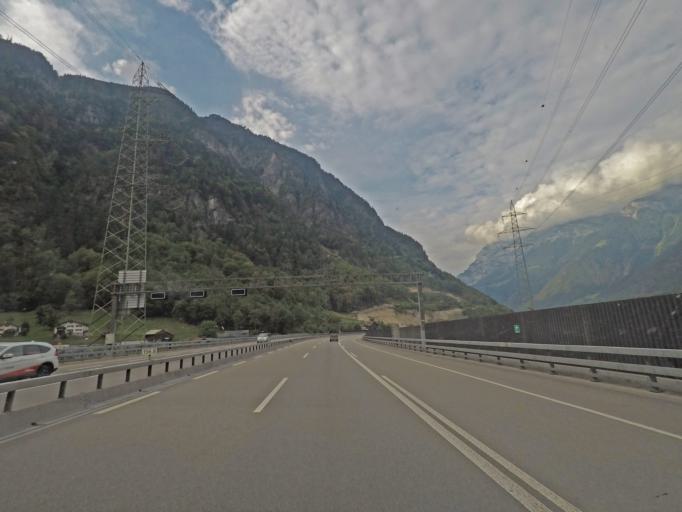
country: CH
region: Uri
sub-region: Uri
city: Silenen
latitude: 46.7739
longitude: 8.6665
